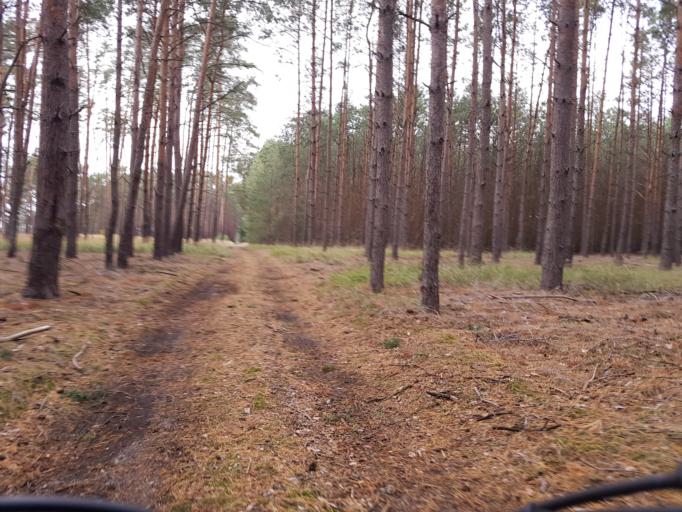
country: DE
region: Brandenburg
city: Schilda
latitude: 51.6165
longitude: 13.3760
